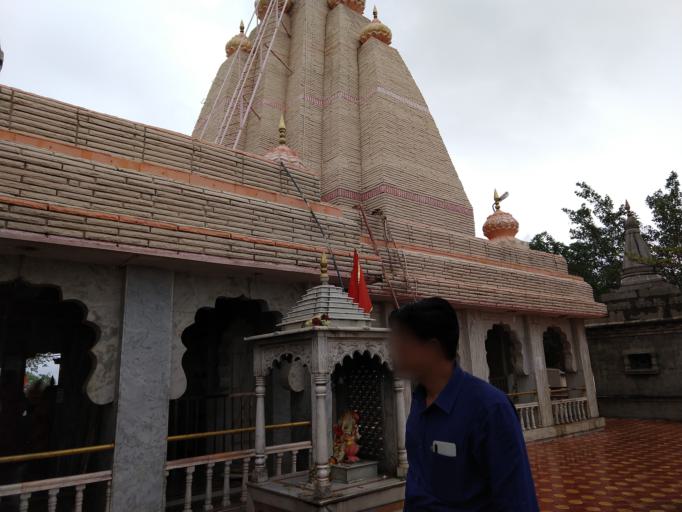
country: IN
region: Maharashtra
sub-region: Pune Division
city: Sasvad
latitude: 18.4143
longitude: 73.9526
